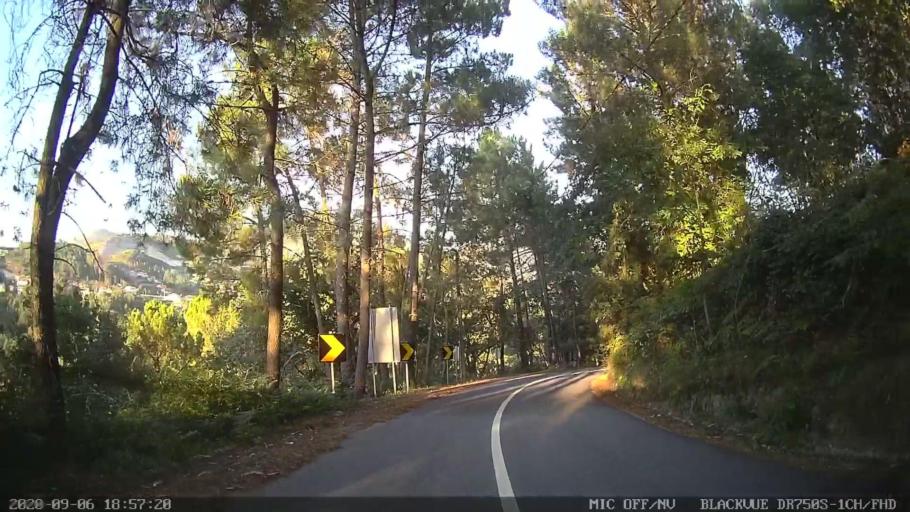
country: PT
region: Porto
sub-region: Baiao
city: Baiao
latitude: 41.2463
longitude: -7.9843
